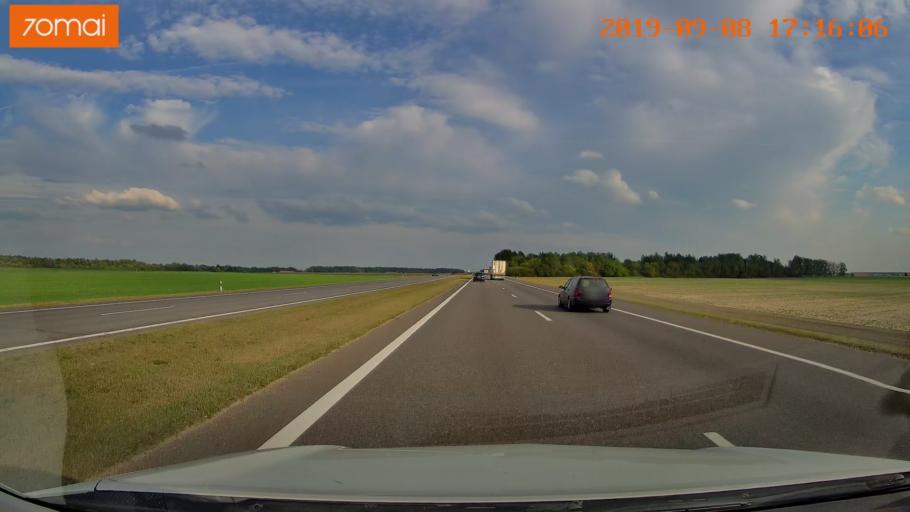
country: BY
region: Grodnenskaya
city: Skidal'
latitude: 53.6031
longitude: 24.1141
